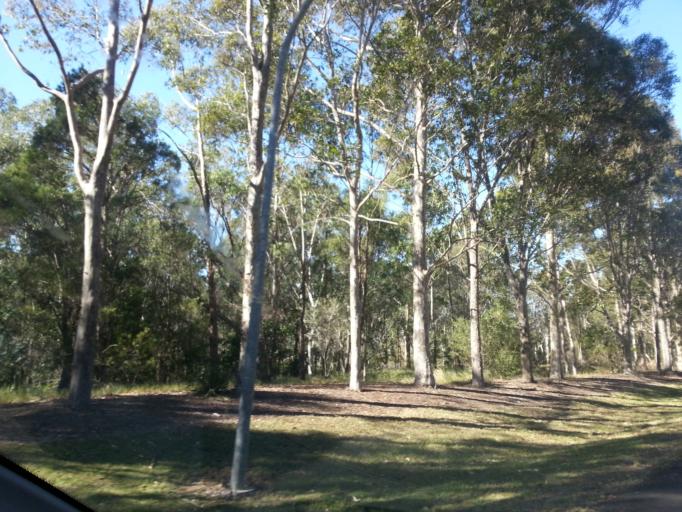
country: AU
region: New South Wales
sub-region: Wollongong
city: Dapto
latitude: -34.5230
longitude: 150.7716
